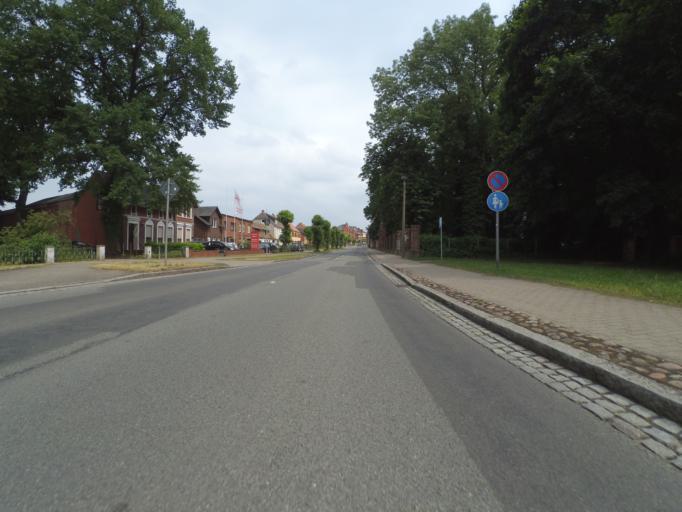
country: DE
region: Mecklenburg-Vorpommern
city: Plau am See
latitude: 53.4594
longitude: 12.2567
